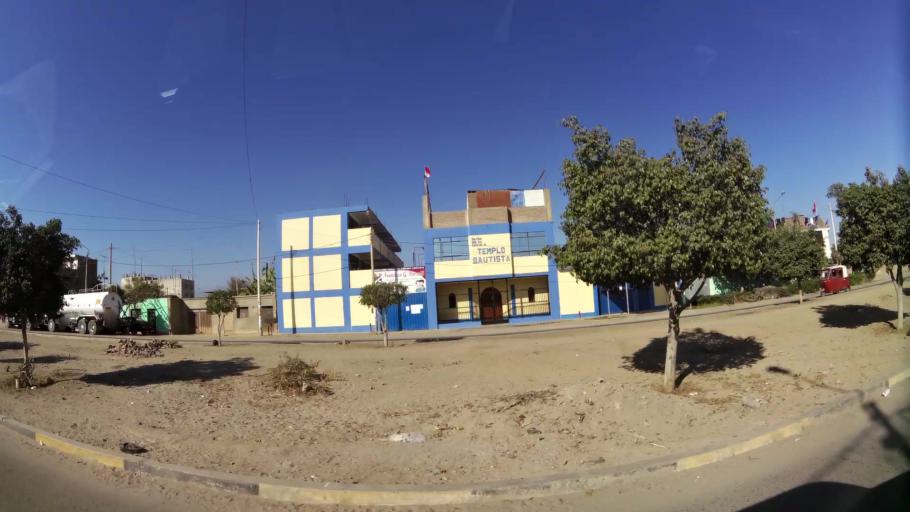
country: PE
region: Ica
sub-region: Provincia de Ica
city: La Tinguina
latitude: -14.0435
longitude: -75.7065
